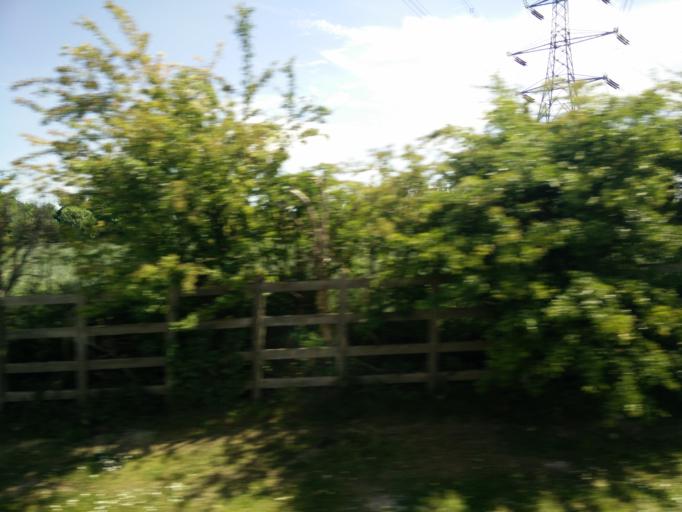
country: GB
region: England
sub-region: Hertfordshire
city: Baldock
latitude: 51.9840
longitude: -0.1994
